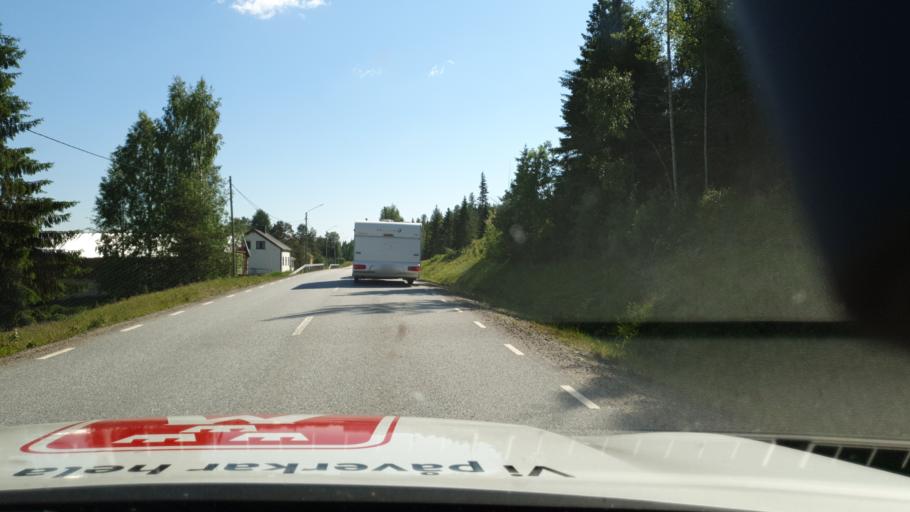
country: SE
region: Vaesterbotten
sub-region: Umea Kommun
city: Ersmark
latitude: 64.3107
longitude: 20.2219
